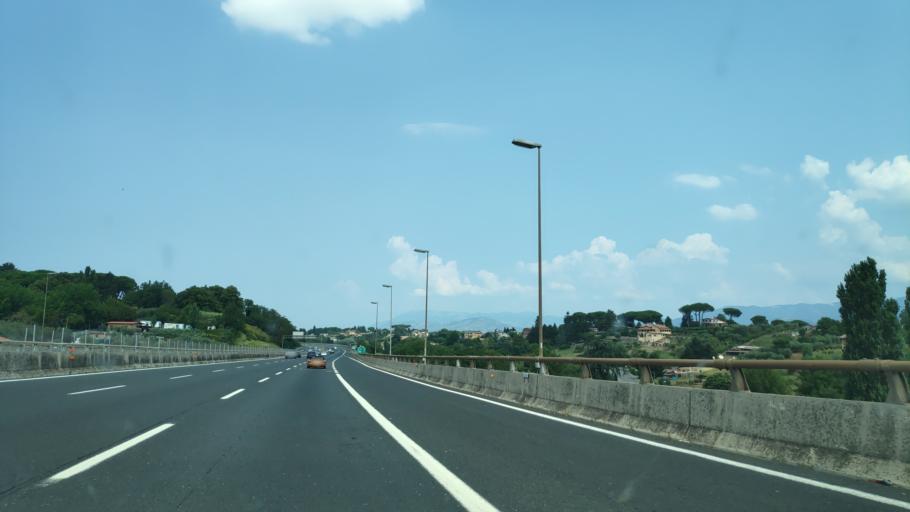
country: IT
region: Latium
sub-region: Citta metropolitana di Roma Capitale
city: San Cesareo
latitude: 41.8132
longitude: 12.8085
